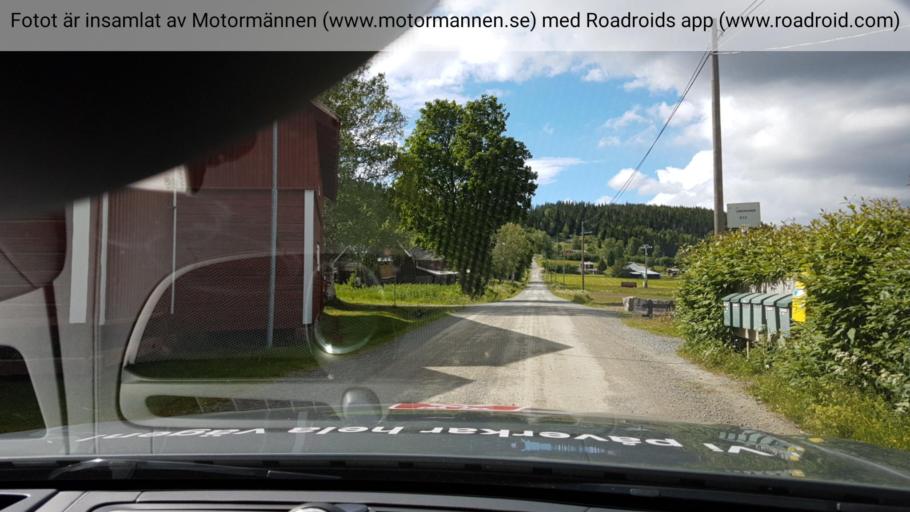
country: SE
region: Jaemtland
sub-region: Bergs Kommun
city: Hoverberg
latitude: 62.9171
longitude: 14.3127
